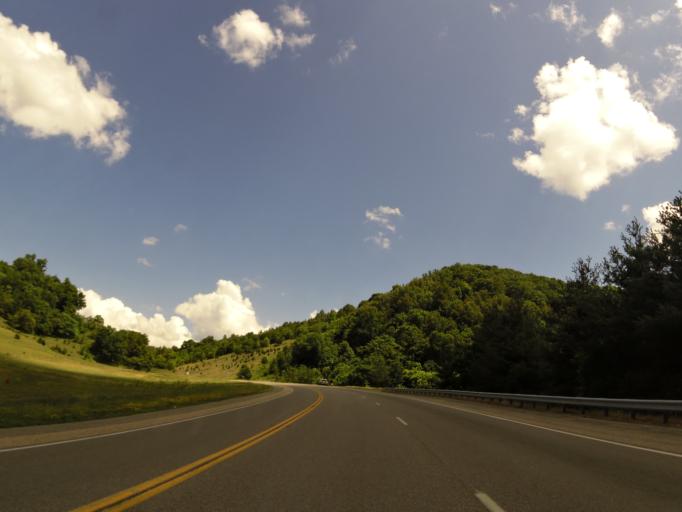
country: US
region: Virginia
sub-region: Lee County
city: Dryden
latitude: 36.7187
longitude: -82.9314
